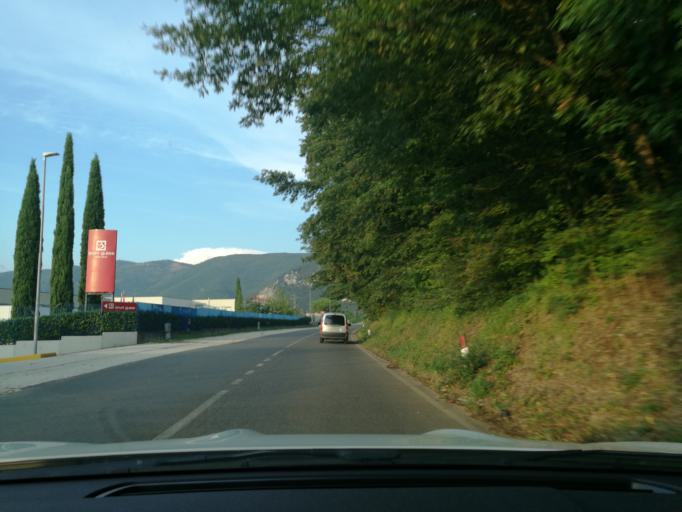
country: IT
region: Umbria
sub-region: Provincia di Terni
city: Acquasparta
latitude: 42.6633
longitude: 12.5432
